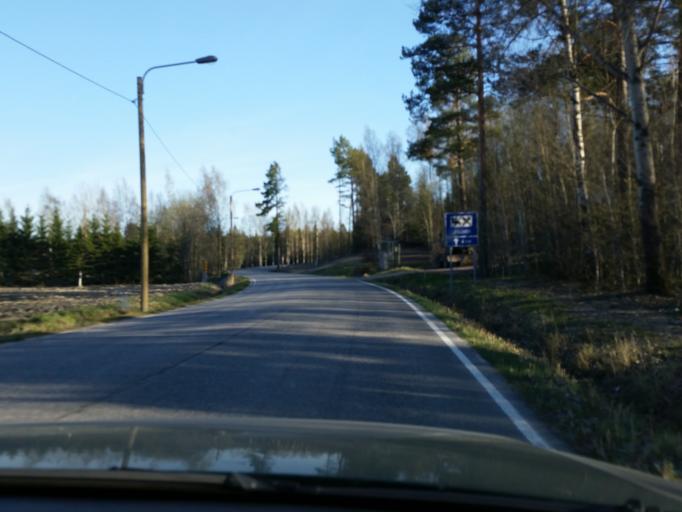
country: FI
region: Uusimaa
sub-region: Helsinki
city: Kirkkonummi
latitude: 60.1300
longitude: 24.5161
